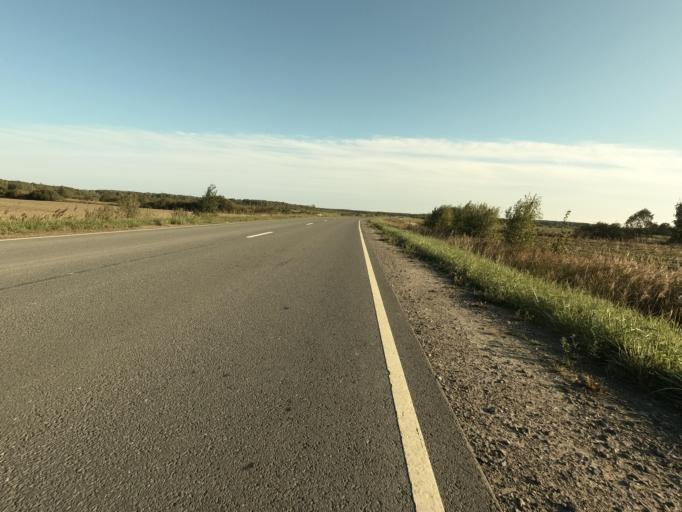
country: RU
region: St.-Petersburg
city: Sapernyy
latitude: 59.7428
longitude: 30.6487
